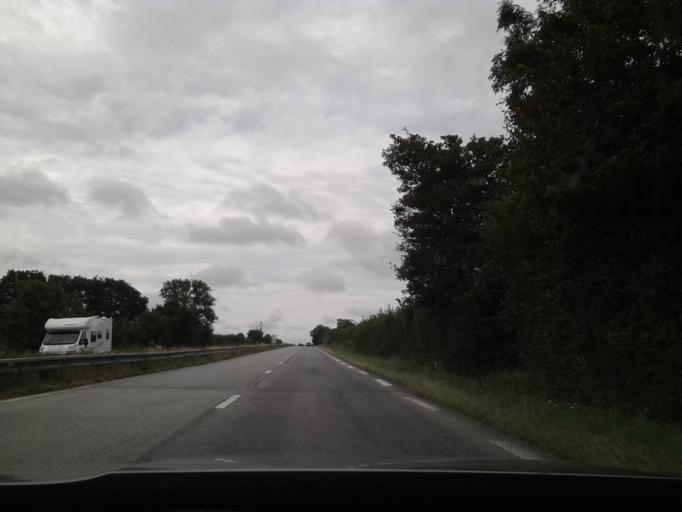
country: FR
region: Lower Normandy
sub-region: Departement de la Manche
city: Carentan
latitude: 49.3563
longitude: -1.2782
